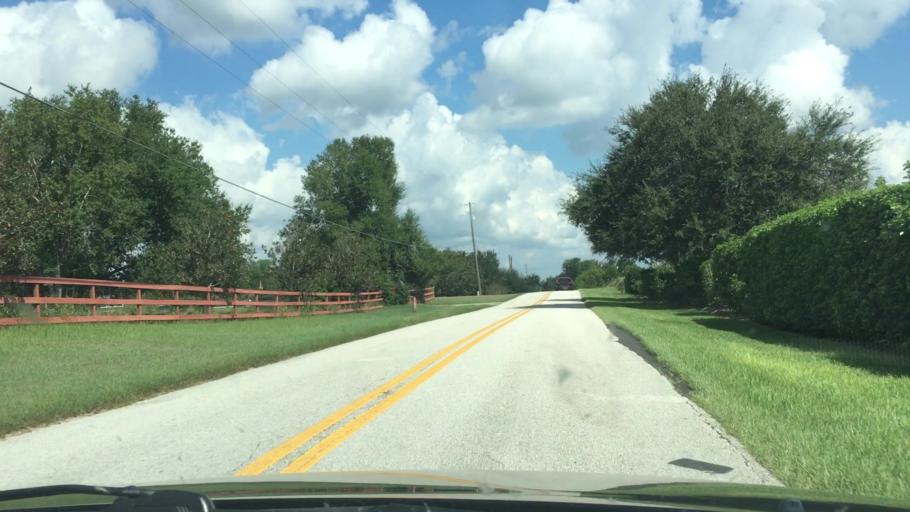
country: US
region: Florida
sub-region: Lake County
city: Montverde
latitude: 28.6022
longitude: -81.6901
